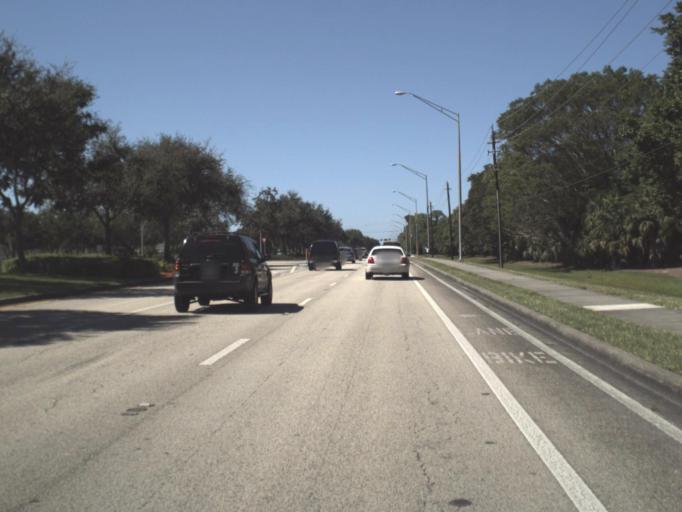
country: US
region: Florida
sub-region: Collier County
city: Lely
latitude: 26.1389
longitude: -81.7468
